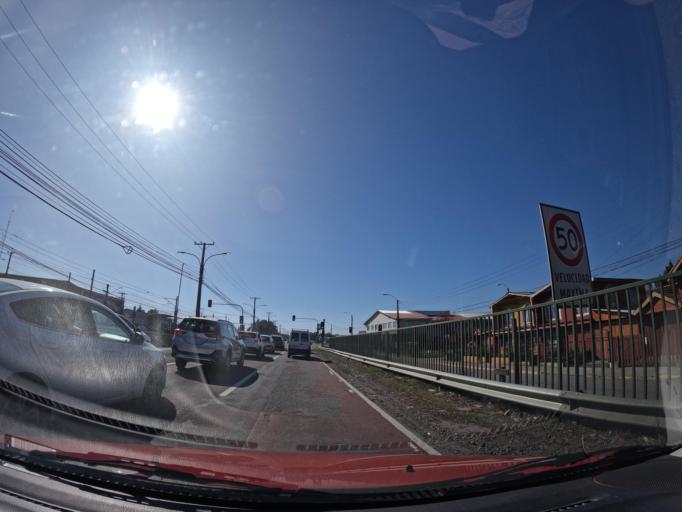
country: CL
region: Biobio
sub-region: Provincia de Concepcion
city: Concepcion
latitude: -36.8487
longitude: -73.1309
